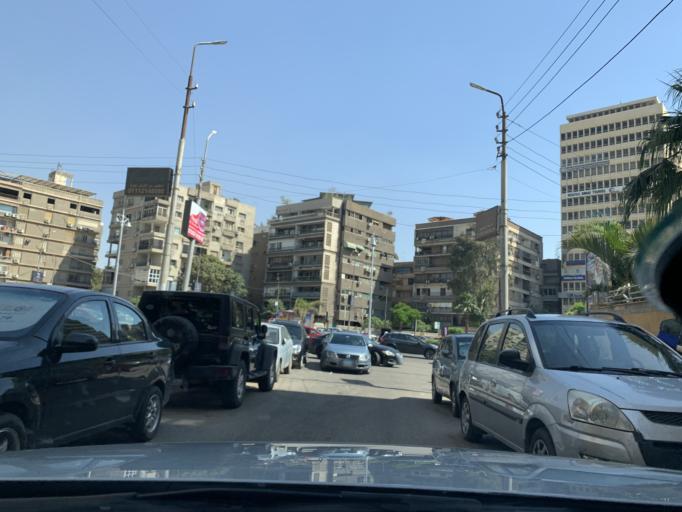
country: EG
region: Muhafazat al Qahirah
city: Cairo
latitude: 30.0854
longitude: 31.3311
